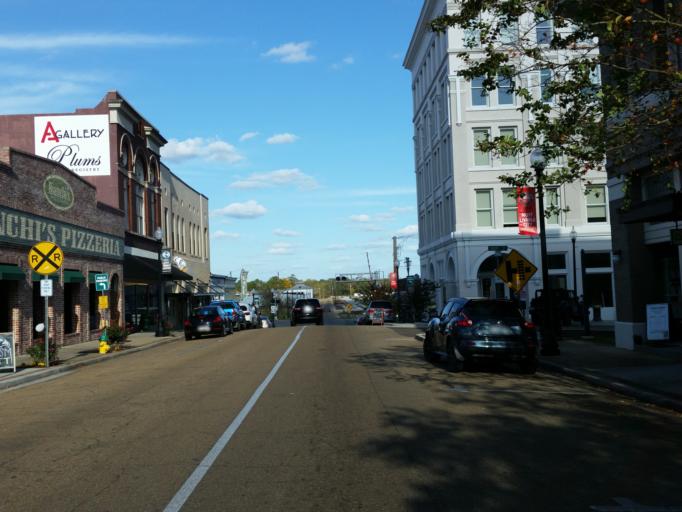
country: US
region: Mississippi
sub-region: Forrest County
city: Hattiesburg
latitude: 31.3268
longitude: -89.2893
